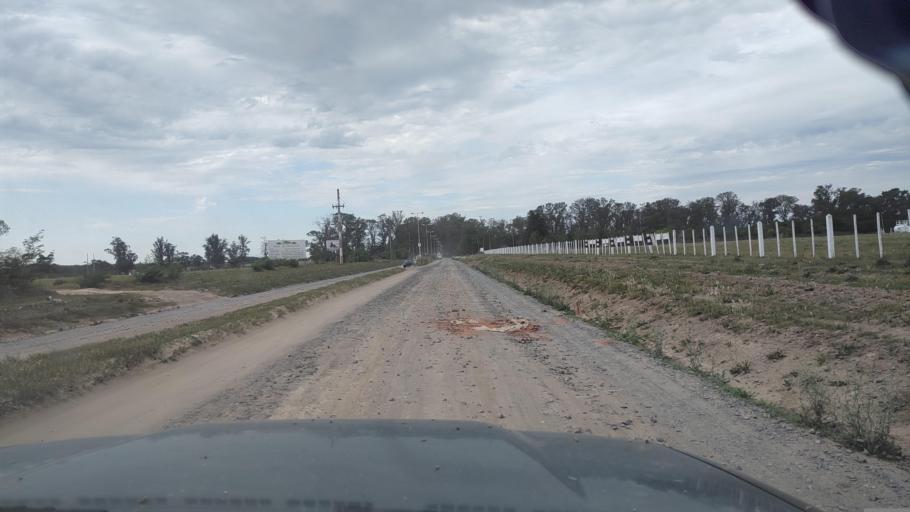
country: AR
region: Buenos Aires
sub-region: Partido de Lujan
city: Lujan
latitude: -34.5475
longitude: -59.0817
